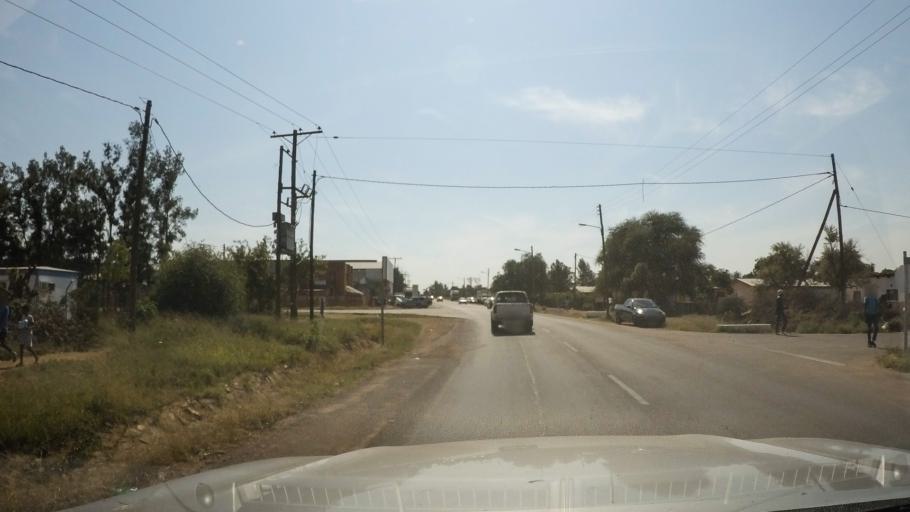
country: BW
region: South East
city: Lobatse
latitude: -25.2060
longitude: 25.6845
